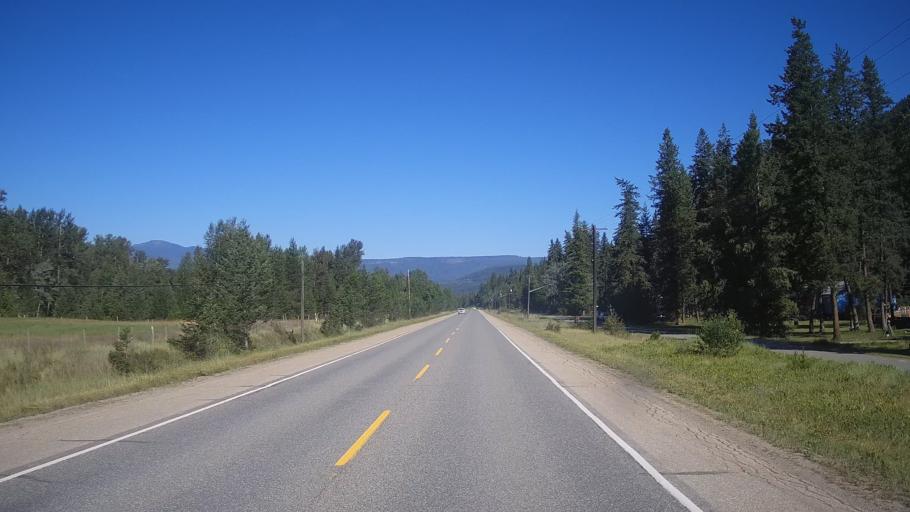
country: CA
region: British Columbia
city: Chase
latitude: 51.6248
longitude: -119.9471
